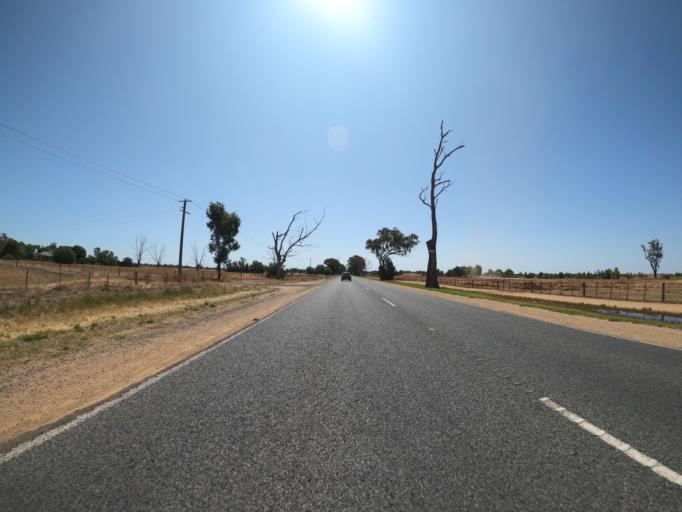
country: AU
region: Victoria
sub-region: Moira
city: Yarrawonga
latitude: -36.0160
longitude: 146.0455
